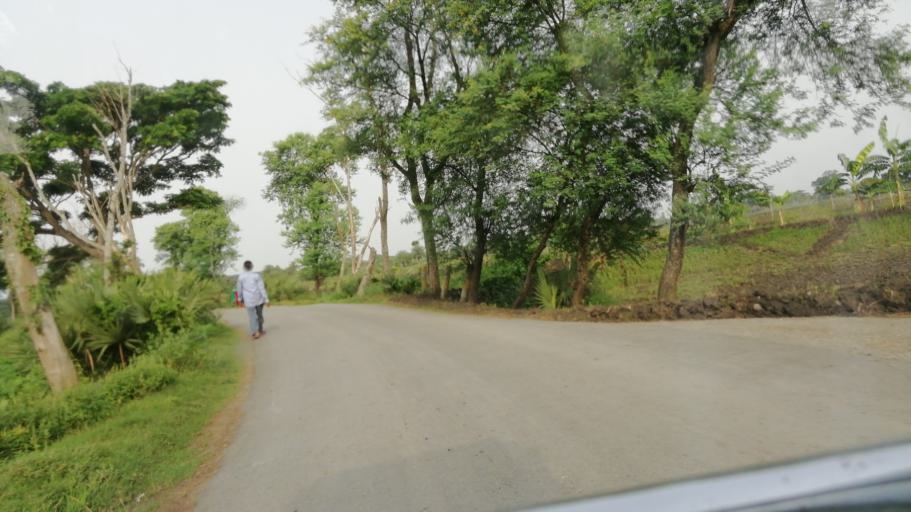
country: BD
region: Khulna
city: Bhatpara Abhaynagar
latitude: 23.0396
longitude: 89.3065
